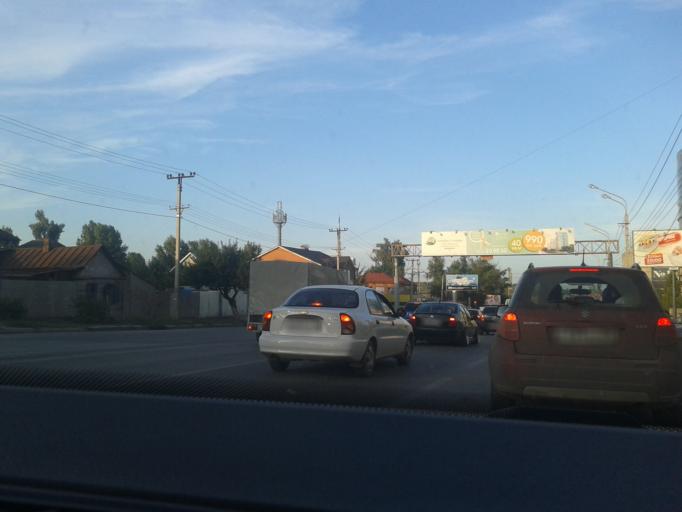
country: RU
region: Volgograd
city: Volgograd
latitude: 48.7276
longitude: 44.5199
